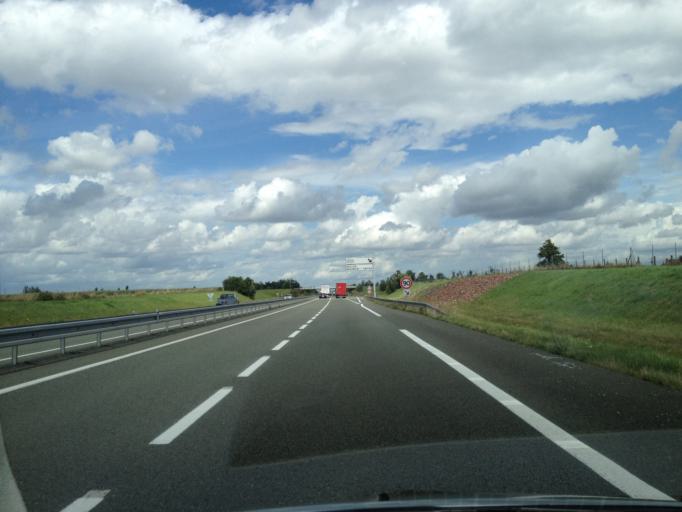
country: FR
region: Pays de la Loire
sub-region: Departement de la Sarthe
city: Montbizot
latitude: 48.1893
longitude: 0.1710
